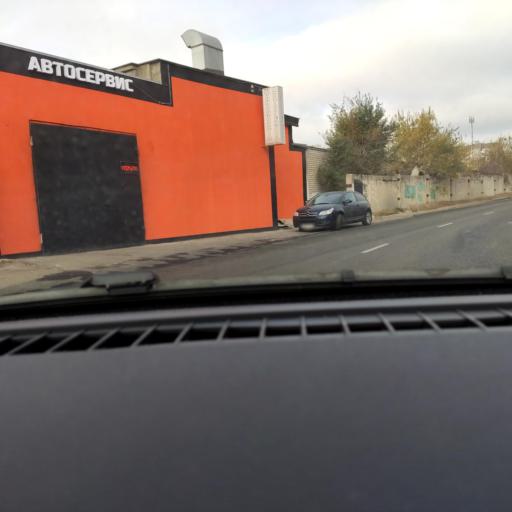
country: RU
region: Voronezj
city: Maslovka
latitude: 51.5905
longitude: 39.2437
